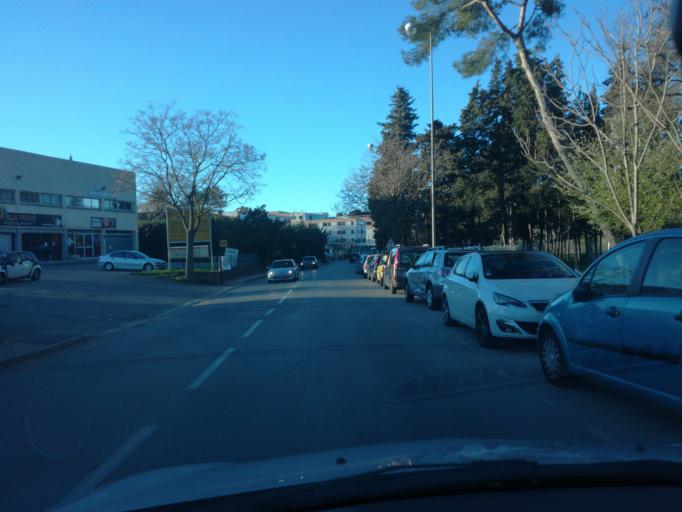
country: FR
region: Provence-Alpes-Cote d'Azur
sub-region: Departement des Alpes-Maritimes
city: La Roquette-sur-Siagne
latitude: 43.6016
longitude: 6.9702
